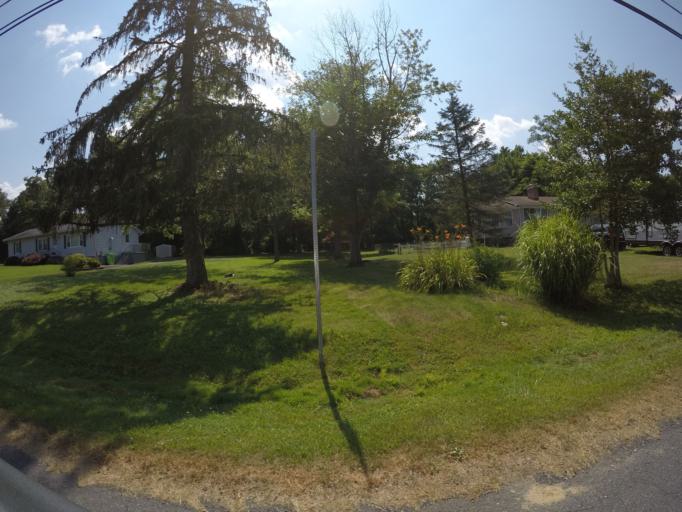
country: US
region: Maryland
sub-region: Harford County
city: Riverside
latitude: 39.4363
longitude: -76.2503
